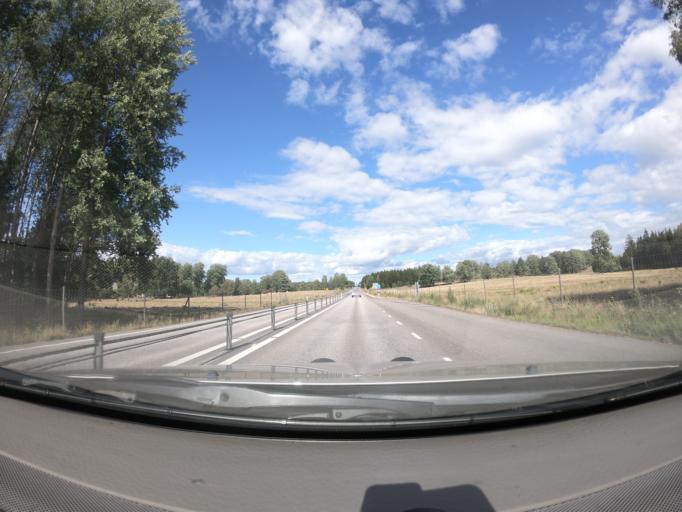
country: SE
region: Kronoberg
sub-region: Vaxjo Kommun
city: Braas
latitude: 57.0313
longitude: 15.0665
